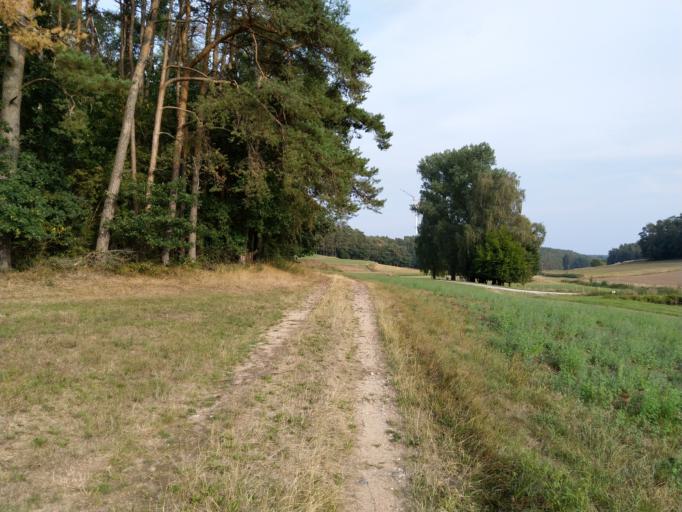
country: DE
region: Bavaria
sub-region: Regierungsbezirk Mittelfranken
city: Hagenbuchach
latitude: 49.5325
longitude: 10.7838
